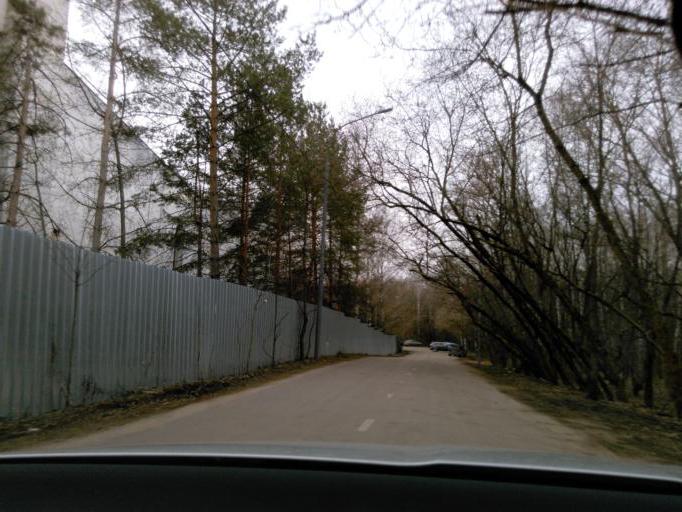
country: RU
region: Moskovskaya
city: Levoberezhnyy
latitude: 55.8275
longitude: 37.4770
